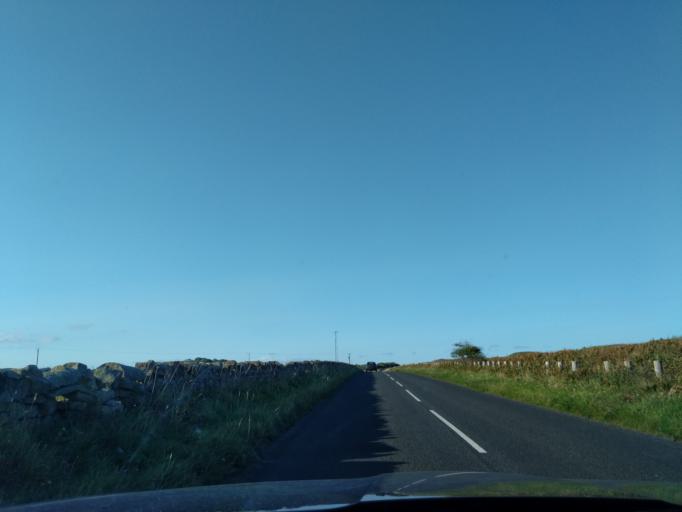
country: GB
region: England
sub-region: Northumberland
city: Lynemouth
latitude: 55.2165
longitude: -1.5297
